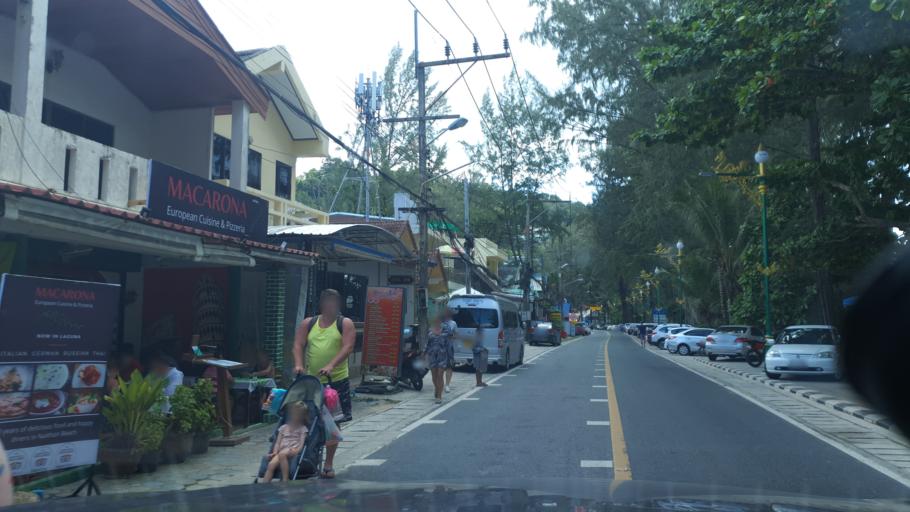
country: TH
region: Phuket
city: Thalang
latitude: 8.0584
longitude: 98.2781
